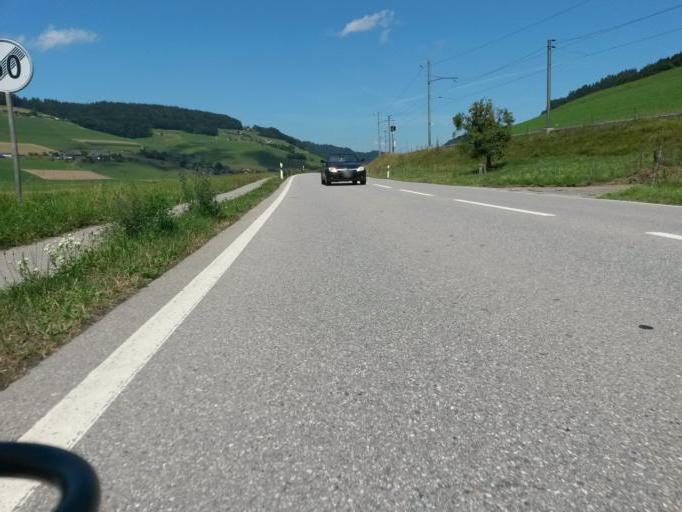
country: CH
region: Bern
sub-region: Bern-Mittelland District
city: Biglen
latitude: 46.9346
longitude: 7.6138
